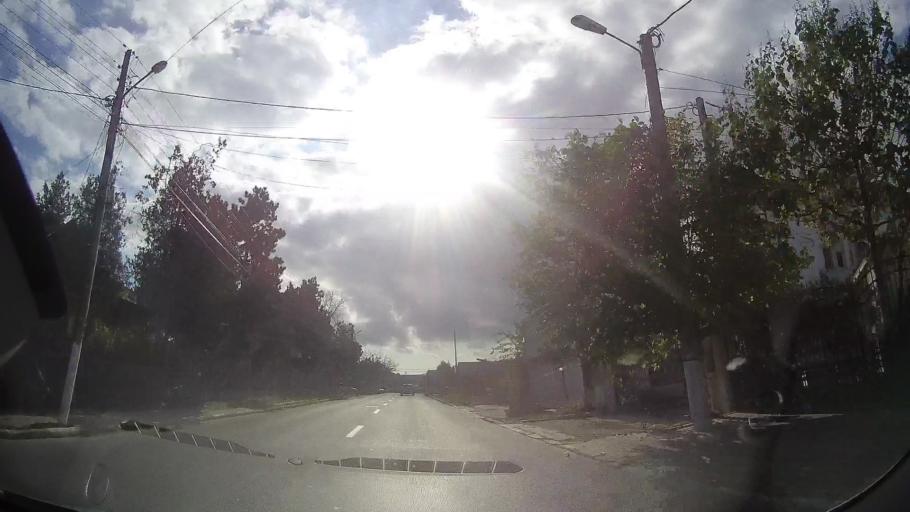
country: RO
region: Constanta
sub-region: Oras Techirghiol
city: Techirghiol
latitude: 44.0605
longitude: 28.5993
